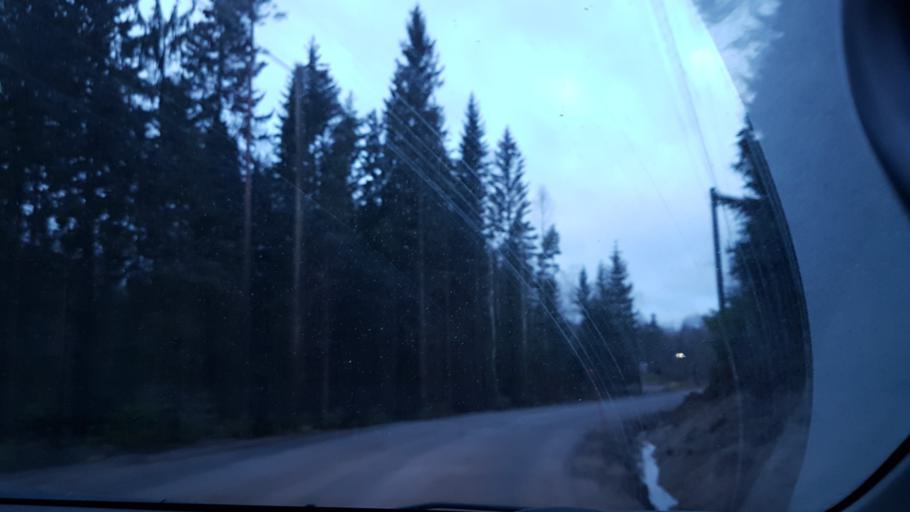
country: FI
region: Uusimaa
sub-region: Helsinki
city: Vantaa
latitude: 60.2851
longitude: 25.1691
